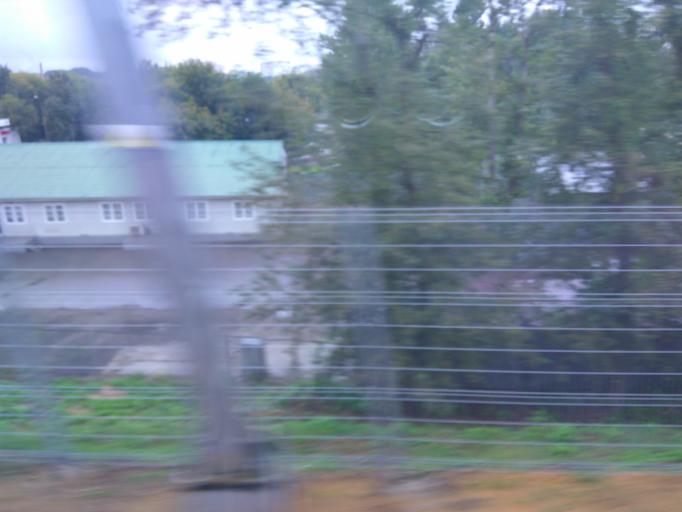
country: RU
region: Moscow
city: Tekstil'shchiki
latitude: 55.7259
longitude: 37.7231
